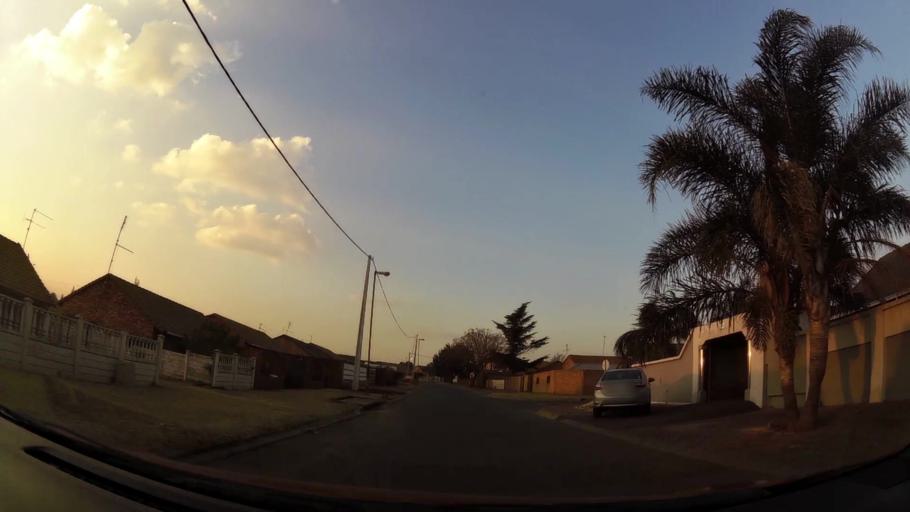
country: ZA
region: Gauteng
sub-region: City of Johannesburg Metropolitan Municipality
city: Soweto
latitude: -26.2884
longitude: 27.8898
